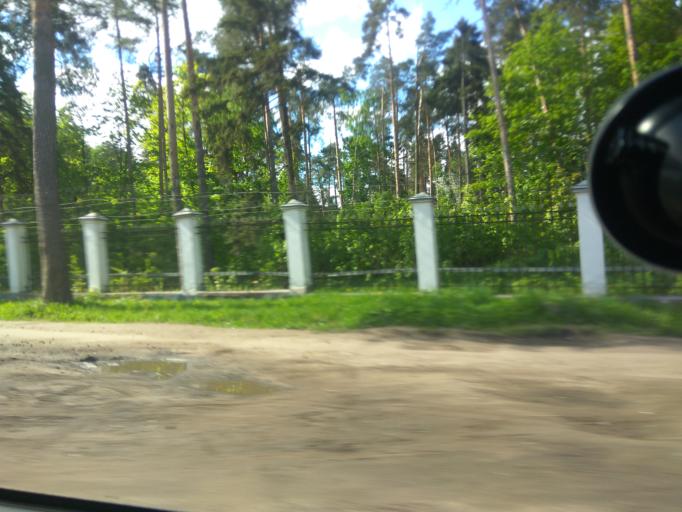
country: RU
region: Moskovskaya
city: Kratovo
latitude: 55.5795
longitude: 38.1541
